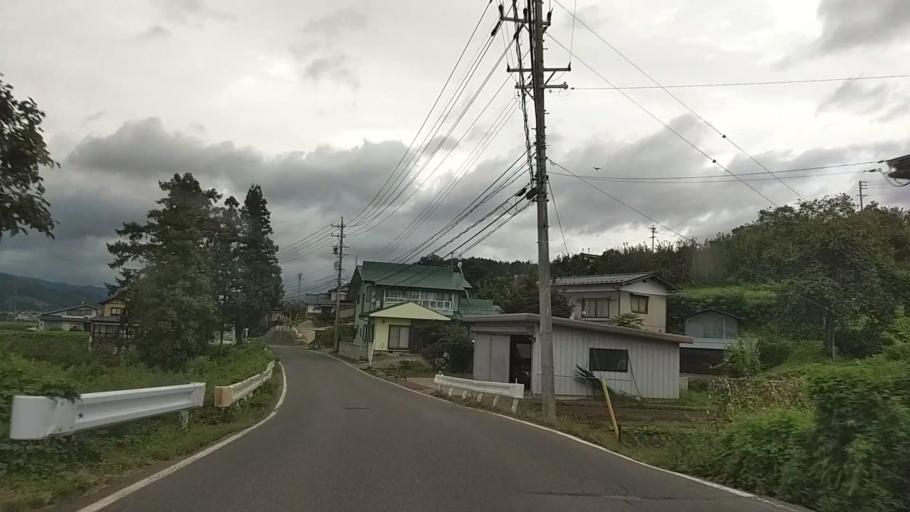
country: JP
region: Nagano
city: Iiyama
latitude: 36.8121
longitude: 138.3604
